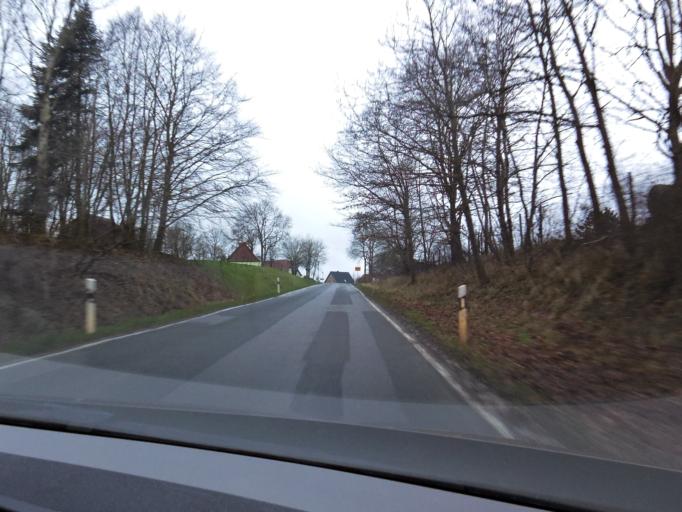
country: DE
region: Mecklenburg-Vorpommern
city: Rehna
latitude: 53.7662
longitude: 11.0976
